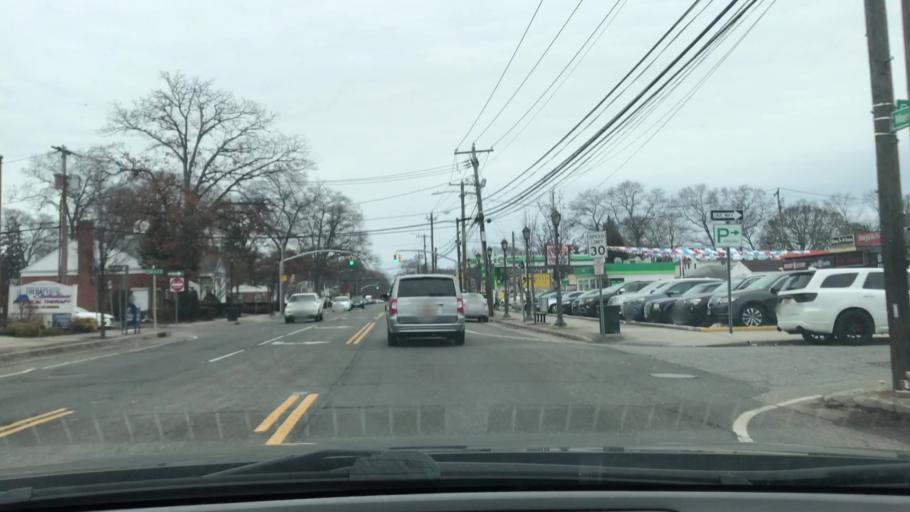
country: US
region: New York
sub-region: Nassau County
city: Merrick
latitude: 40.6757
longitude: -73.5572
